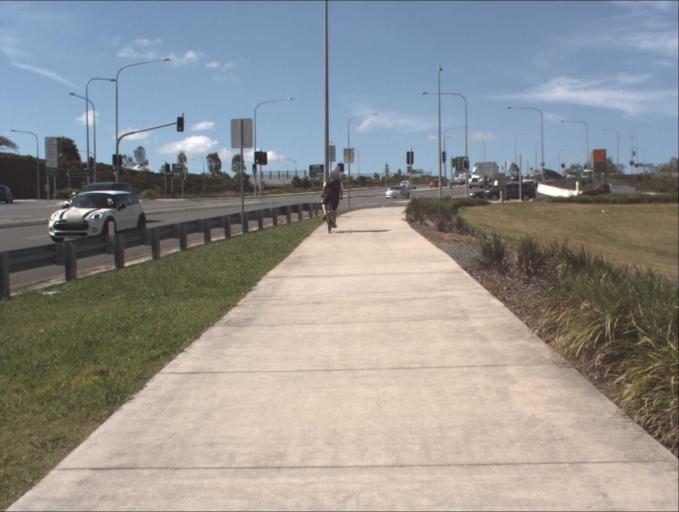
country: AU
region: Queensland
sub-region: Logan
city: Slacks Creek
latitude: -27.6461
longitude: 153.1444
